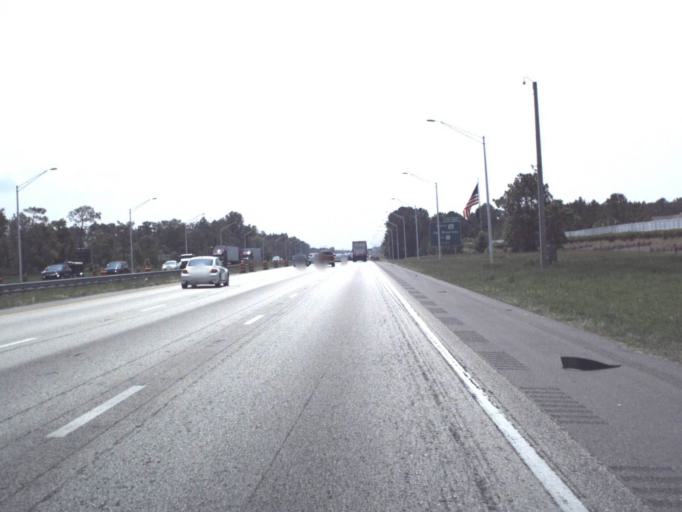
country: US
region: Florida
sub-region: Saint Johns County
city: Fruit Cove
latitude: 30.1310
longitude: -81.5306
